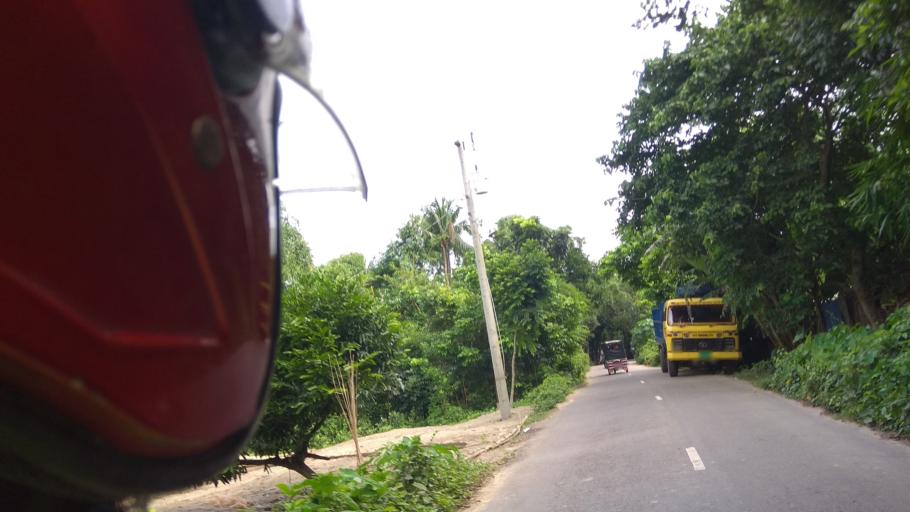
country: BD
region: Khulna
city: Kalia
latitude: 23.1630
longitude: 89.6443
